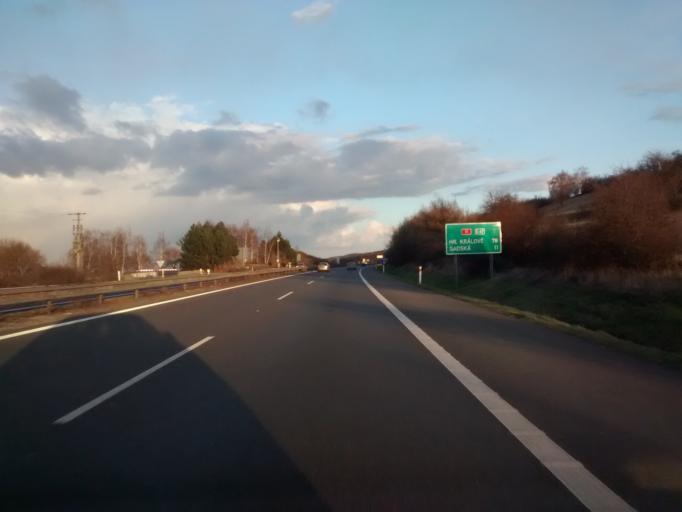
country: CZ
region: Central Bohemia
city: Prerov nad Labem
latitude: 50.1355
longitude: 14.8530
